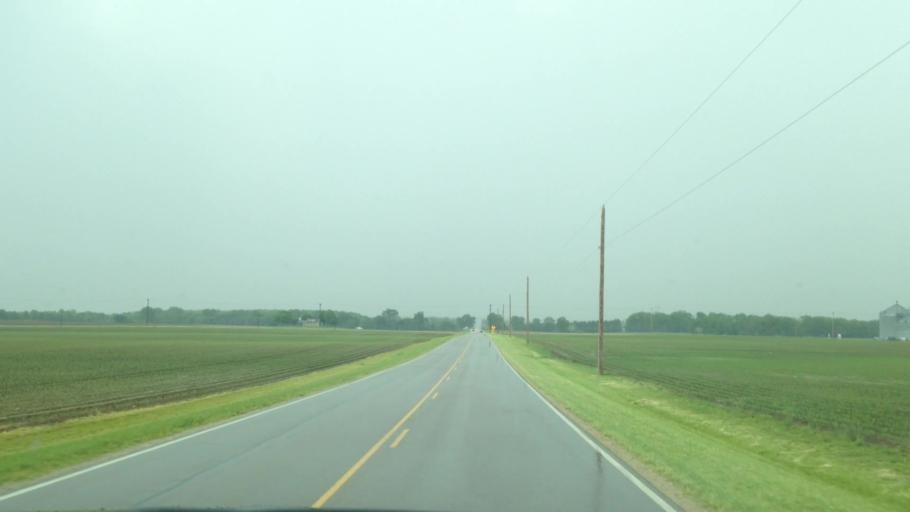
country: US
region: Ohio
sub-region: Darke County
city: Greenville
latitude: 40.1504
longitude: -84.6423
